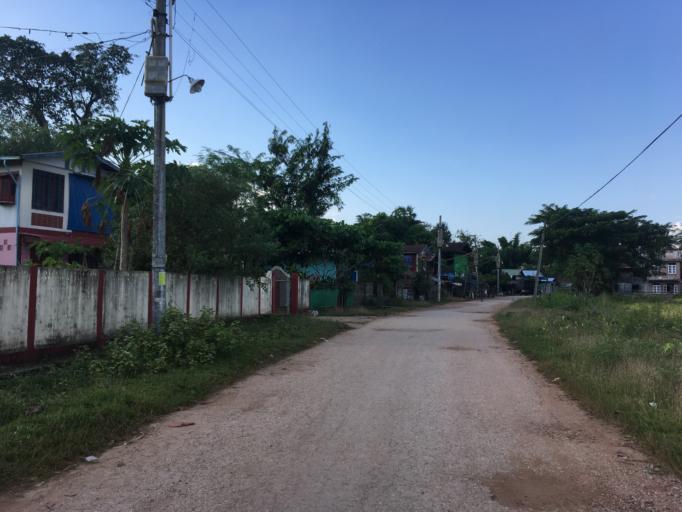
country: MM
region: Mon
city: Mawlamyine
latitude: 16.4318
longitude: 97.6211
